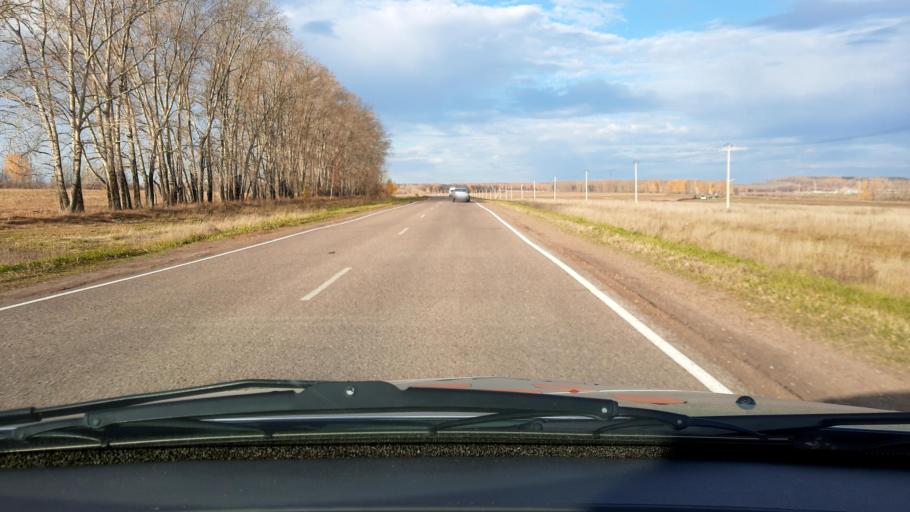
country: RU
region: Bashkortostan
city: Mikhaylovka
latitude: 54.8170
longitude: 55.7818
